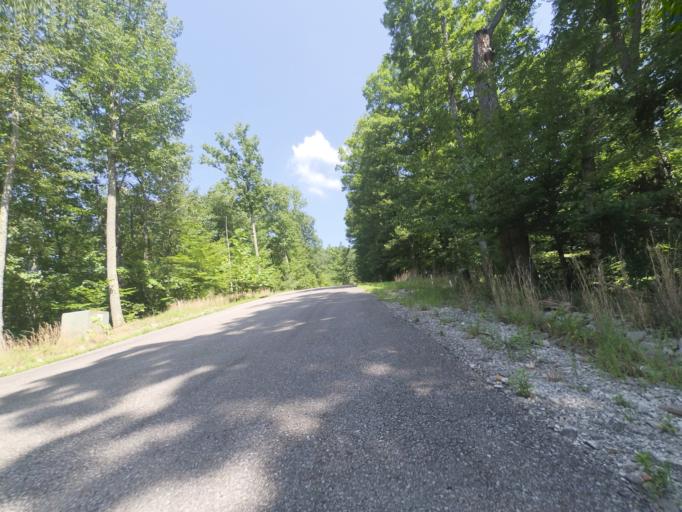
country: US
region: West Virginia
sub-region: Cabell County
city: Huntington
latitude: 38.3818
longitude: -82.4641
